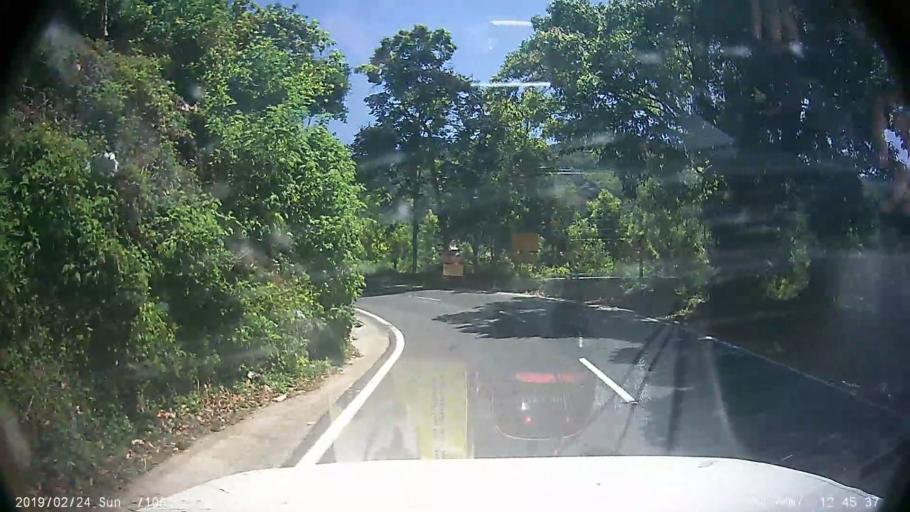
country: IN
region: Tamil Nadu
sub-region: Nilgiri
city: Wellington
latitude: 11.3343
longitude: 76.7921
